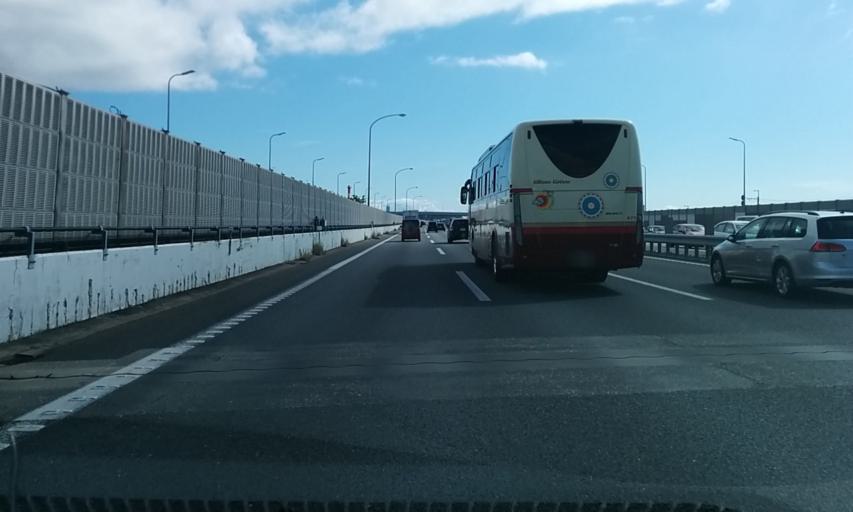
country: JP
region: Hyogo
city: Kawanishi
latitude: 34.8112
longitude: 135.4111
